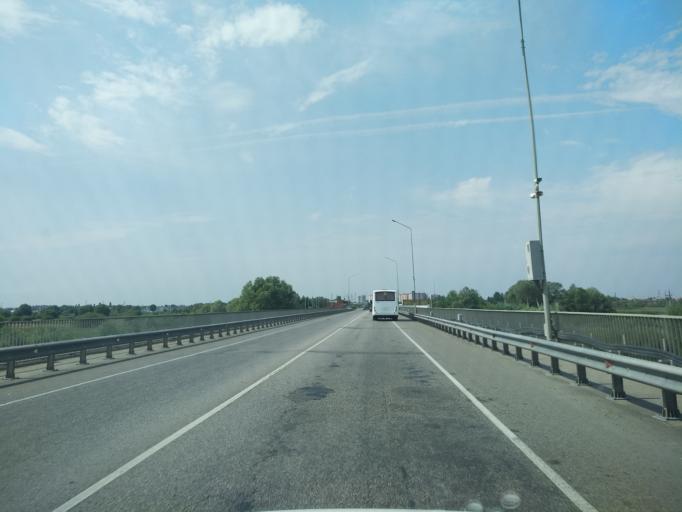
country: RU
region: Voronezj
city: Somovo
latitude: 51.6835
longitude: 39.3482
